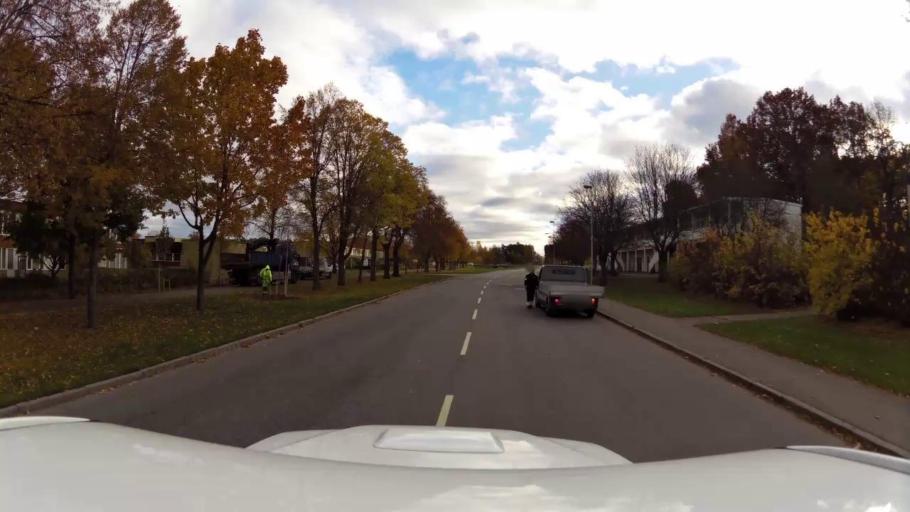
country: SE
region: OEstergoetland
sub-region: Linkopings Kommun
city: Malmslatt
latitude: 58.4071
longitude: 15.5656
